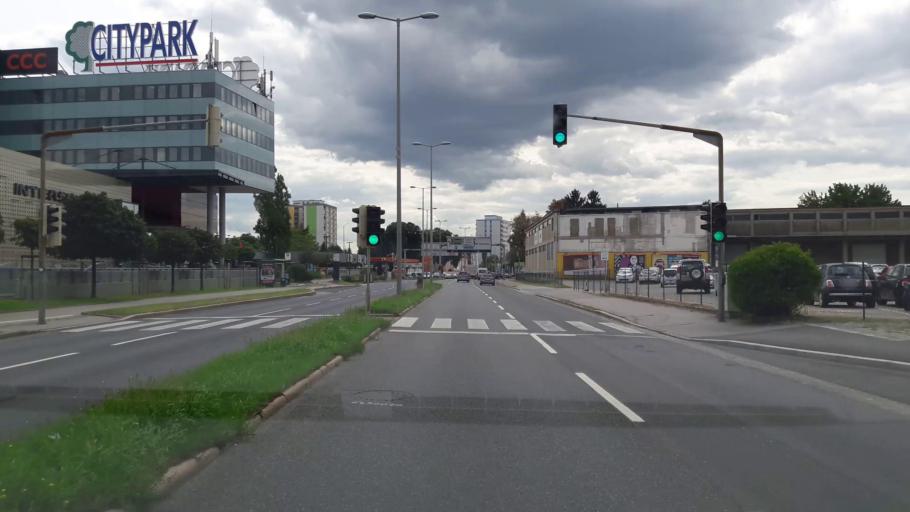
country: AT
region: Styria
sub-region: Graz Stadt
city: Graz
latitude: 47.0606
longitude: 15.4253
